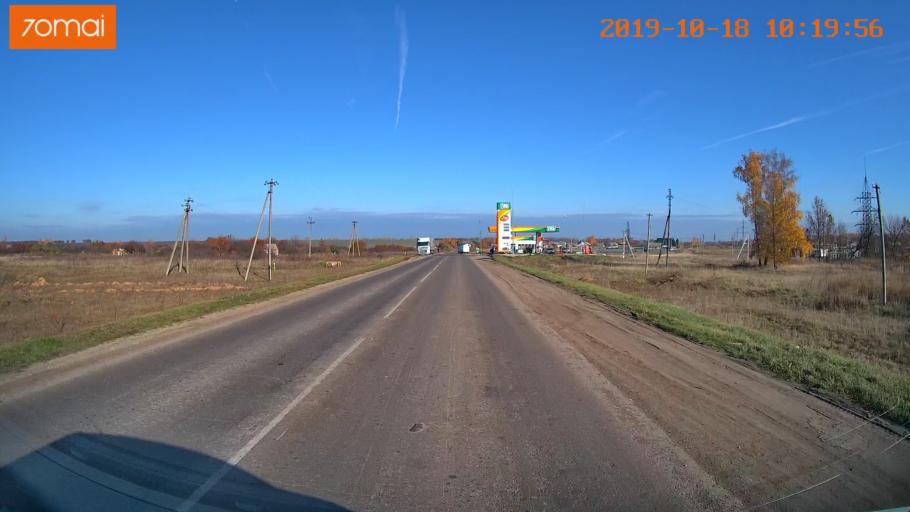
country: RU
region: Tula
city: Kurkino
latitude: 53.4253
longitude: 38.6448
